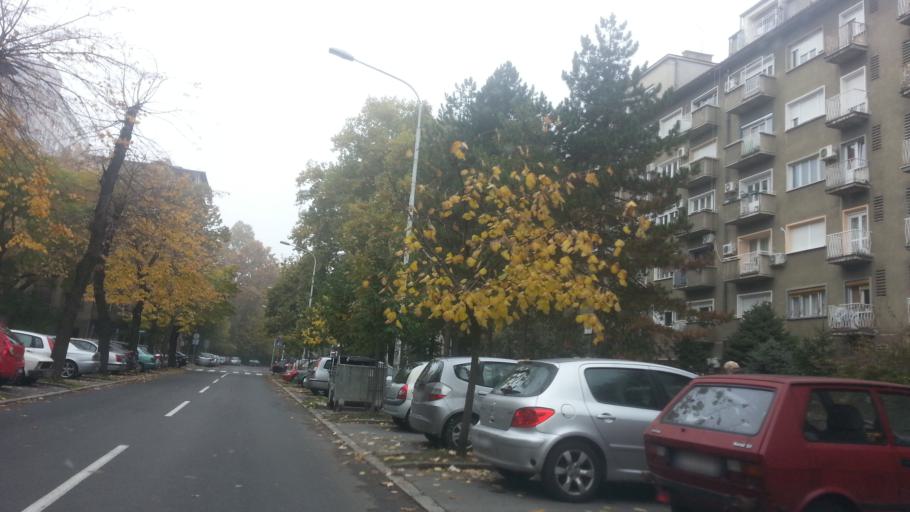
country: RS
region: Central Serbia
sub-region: Belgrade
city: Zemun
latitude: 44.8329
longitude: 20.4048
